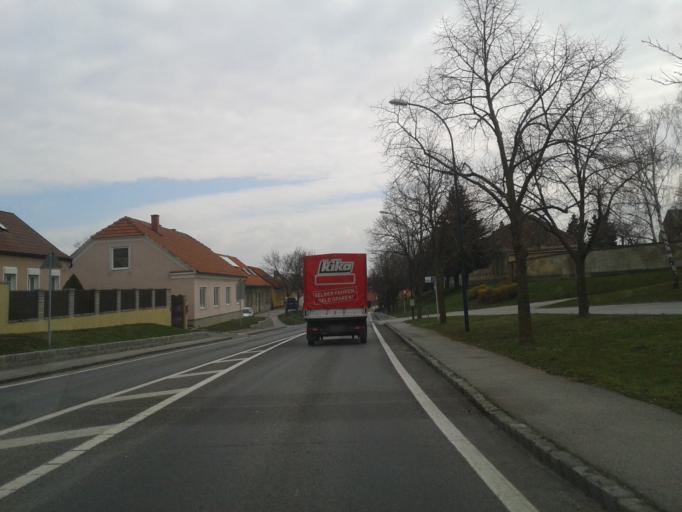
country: AT
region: Lower Austria
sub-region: Politischer Bezirk Bruck an der Leitha
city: Scharndorf
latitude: 48.1089
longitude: 16.7753
